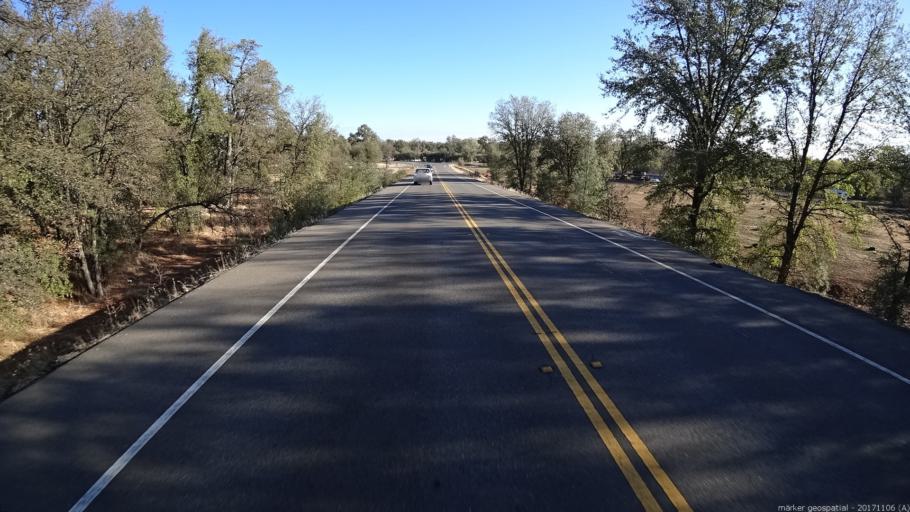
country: US
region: California
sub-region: Shasta County
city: Palo Cedro
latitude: 40.5943
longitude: -122.2365
